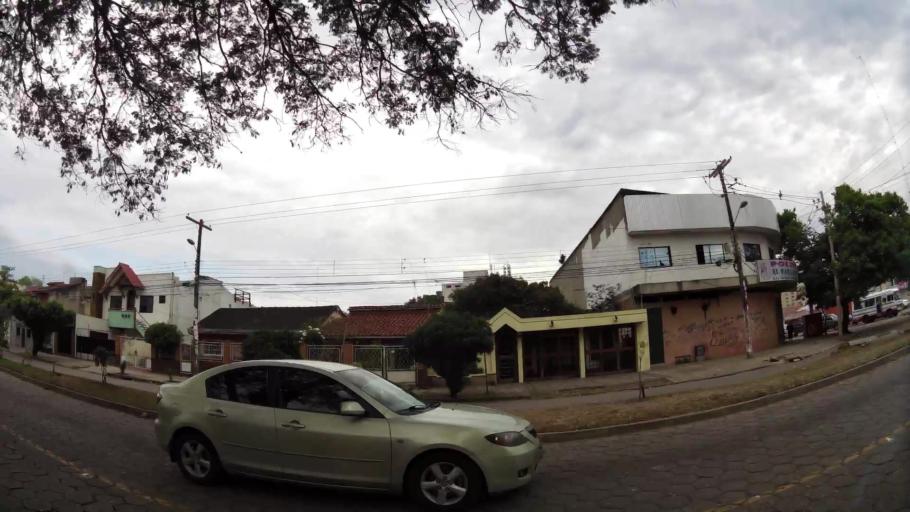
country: BO
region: Santa Cruz
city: Santa Cruz de la Sierra
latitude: -17.7719
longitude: -63.1685
